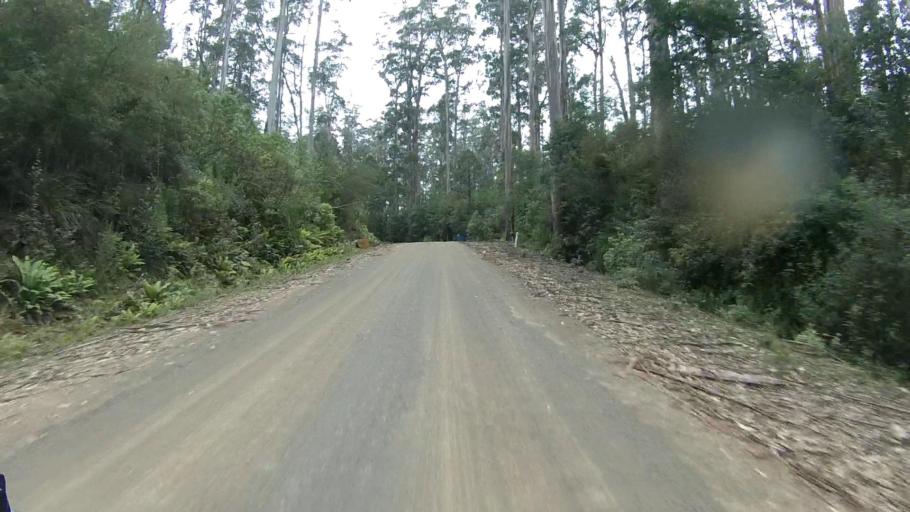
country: AU
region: Tasmania
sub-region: Sorell
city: Sorell
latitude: -42.7027
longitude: 147.8562
